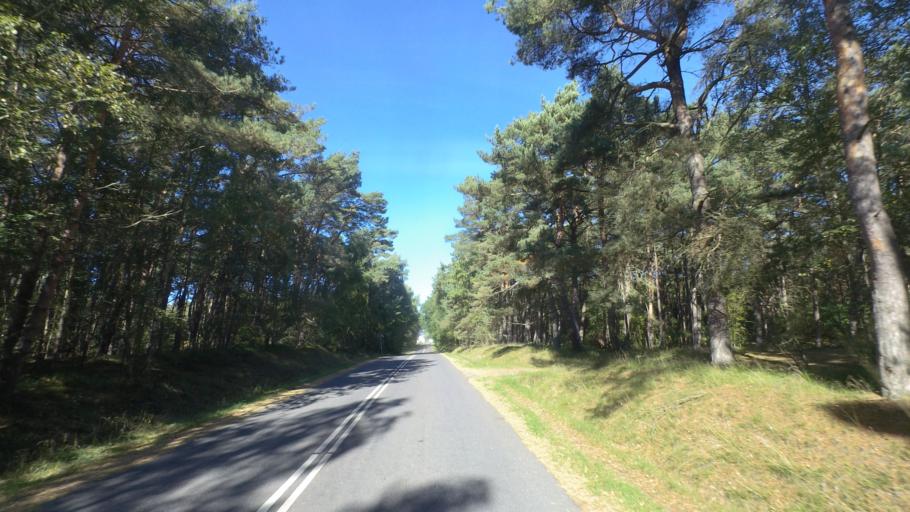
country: DK
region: Capital Region
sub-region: Bornholm Kommune
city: Nexo
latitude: 54.9995
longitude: 15.0757
